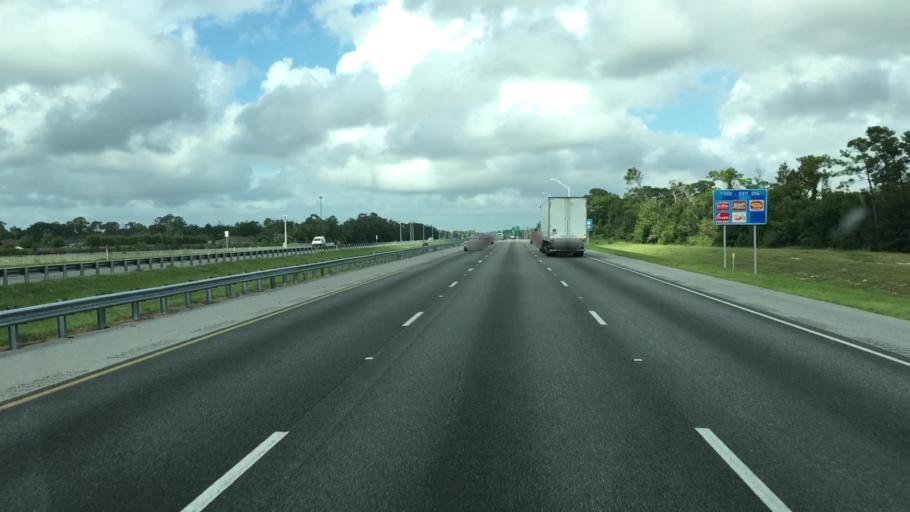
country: US
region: Florida
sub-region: Volusia County
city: Port Orange
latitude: 29.0952
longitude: -81.0231
